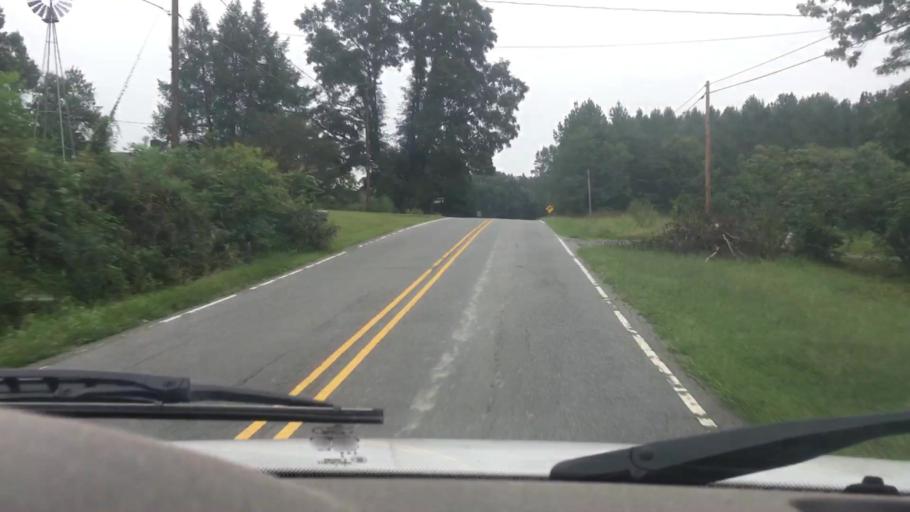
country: US
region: North Carolina
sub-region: Gaston County
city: Davidson
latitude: 35.4665
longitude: -80.7568
